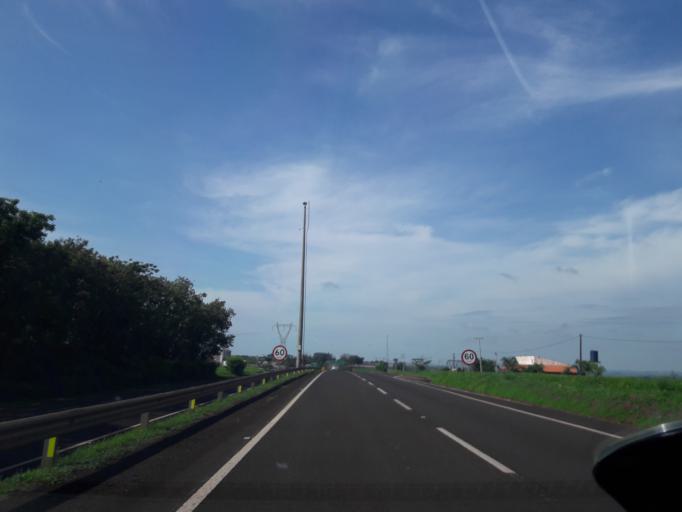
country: BR
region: Parana
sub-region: Paicandu
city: Paicandu
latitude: -23.5998
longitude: -52.0802
